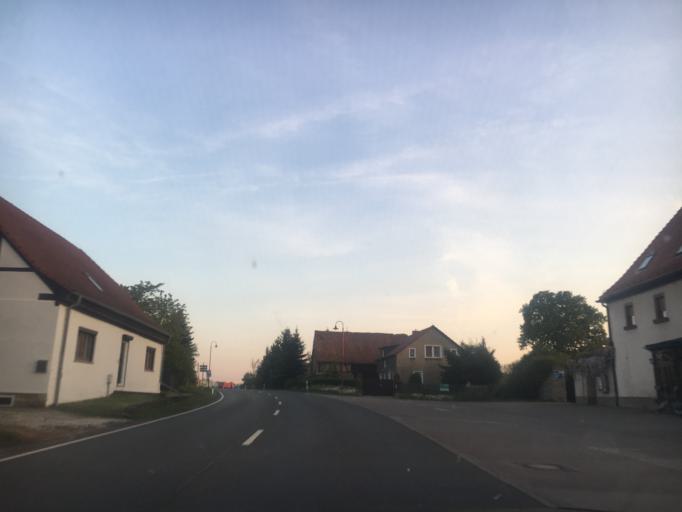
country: DE
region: Thuringia
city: Hirschfeld
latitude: 50.9663
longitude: 12.1334
